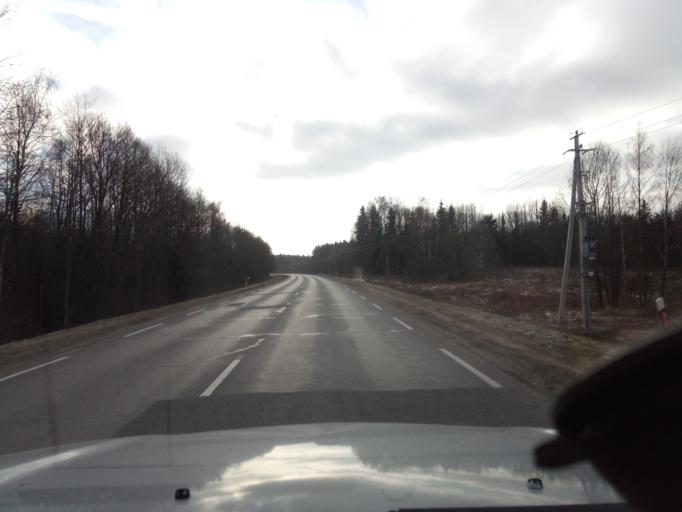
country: LT
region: Alytaus apskritis
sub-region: Alytus
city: Alytus
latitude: 54.3169
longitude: 24.1403
